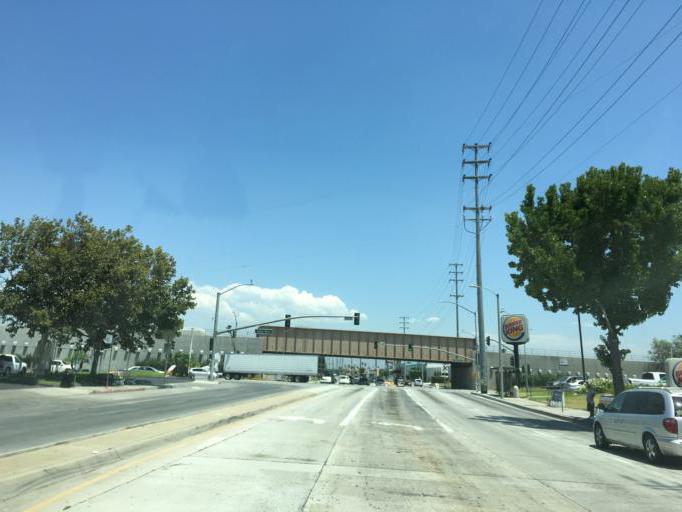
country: US
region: California
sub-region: Los Angeles County
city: Avocado Heights
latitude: 34.0342
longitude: -117.9754
